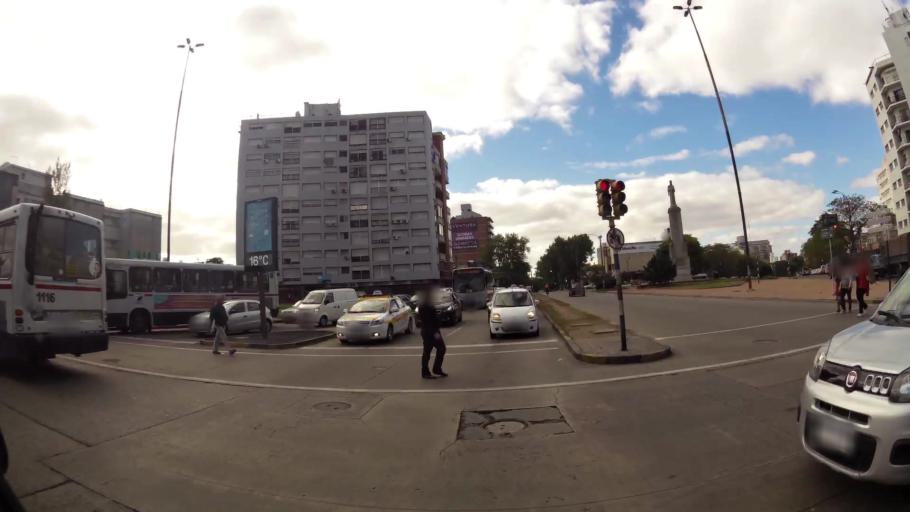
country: UY
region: Montevideo
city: Montevideo
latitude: -34.8820
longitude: -56.1524
